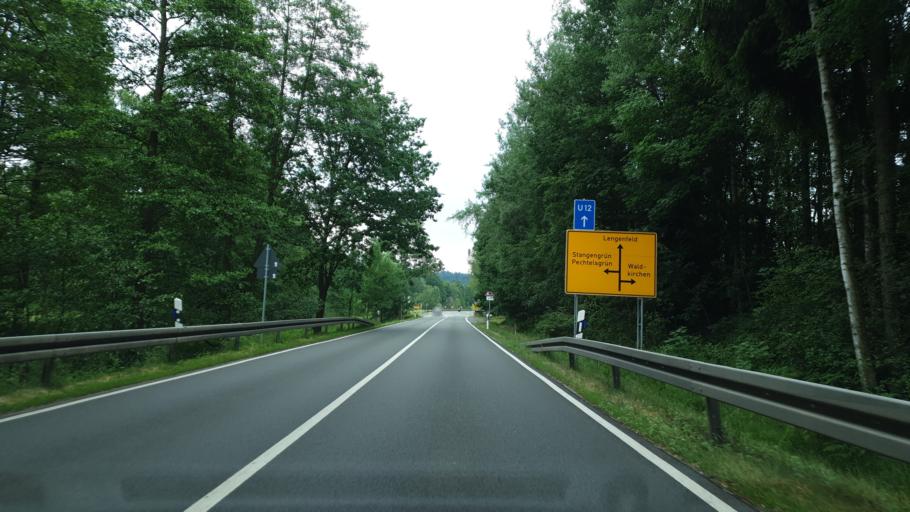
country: DE
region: Saxony
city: Waldkirchen
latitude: 50.5944
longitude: 12.3993
